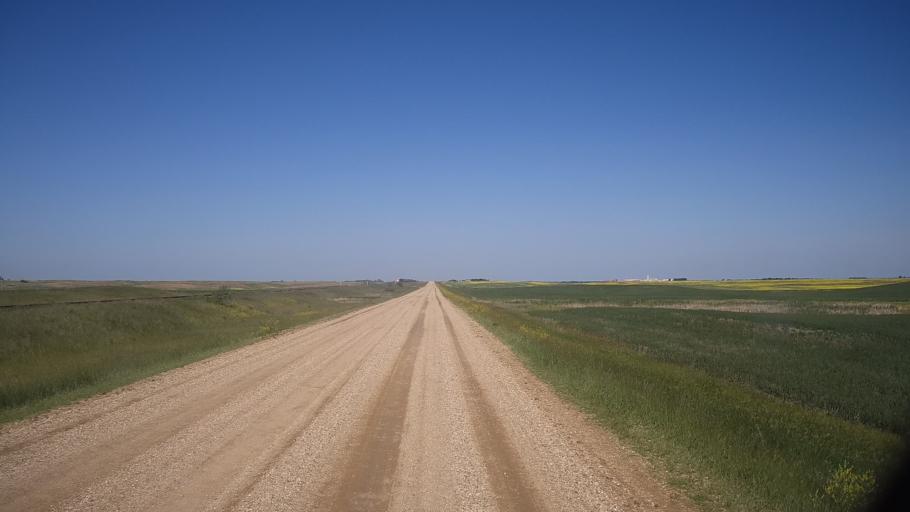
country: CA
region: Saskatchewan
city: Watrous
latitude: 51.8533
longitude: -105.9424
